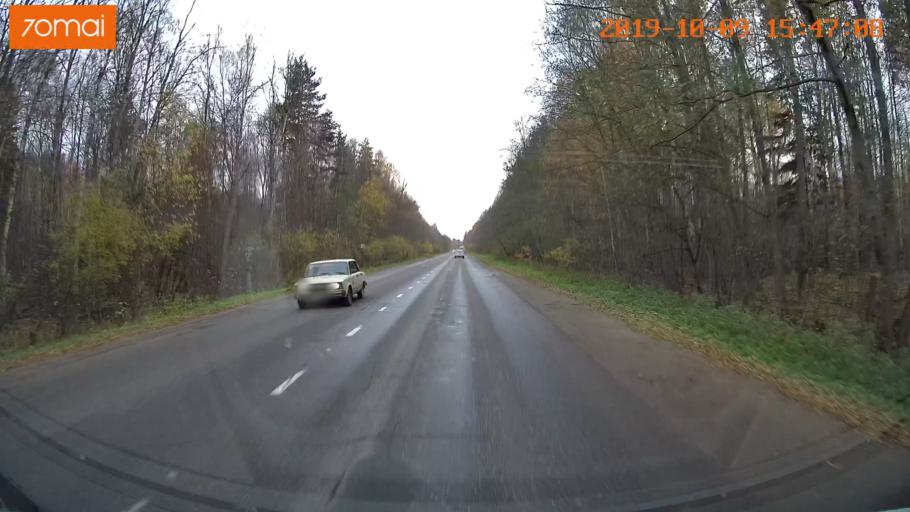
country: RU
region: Kostroma
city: Oktyabr'skiy
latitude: 57.8196
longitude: 41.0332
